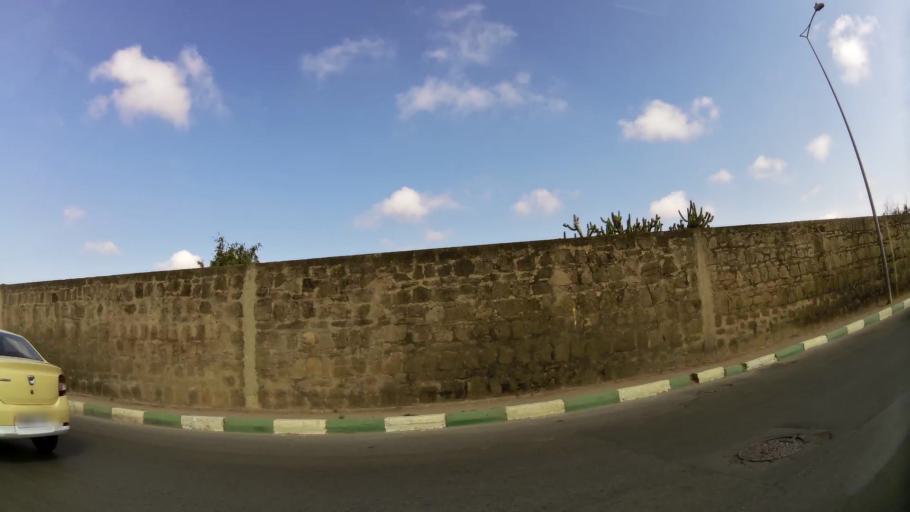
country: MA
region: Rabat-Sale-Zemmour-Zaer
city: Sale
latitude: 34.0587
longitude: -6.7695
